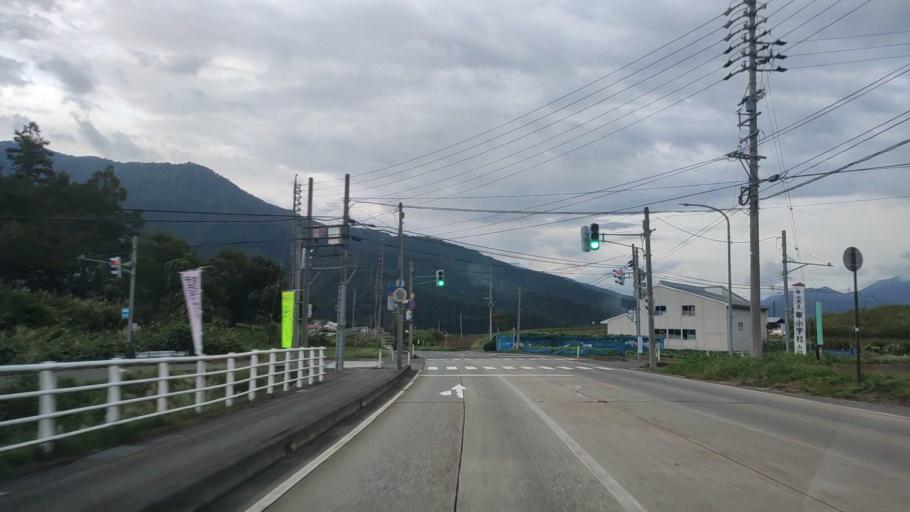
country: JP
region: Nagano
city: Iiyama
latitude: 36.8866
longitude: 138.4100
